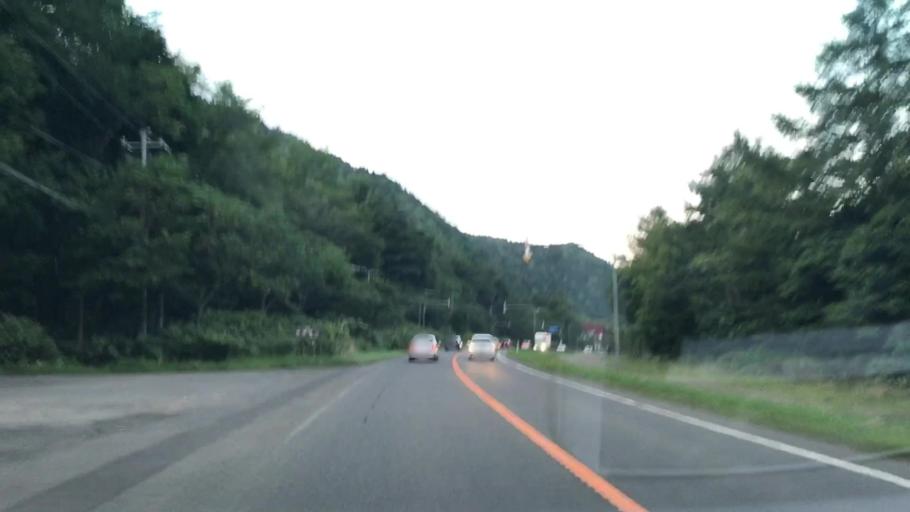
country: JP
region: Hokkaido
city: Sapporo
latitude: 42.9406
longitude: 141.1267
